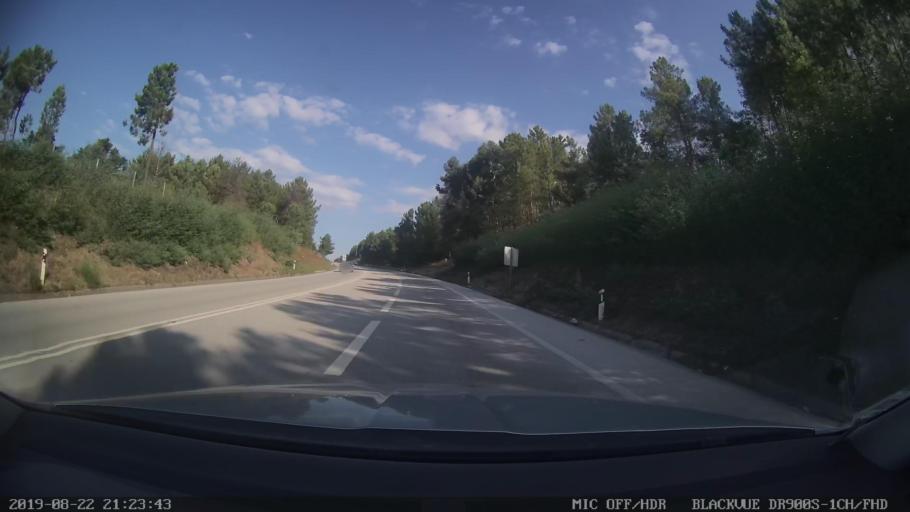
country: PT
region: Castelo Branco
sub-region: Serta
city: Serta
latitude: 39.8344
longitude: -8.1115
